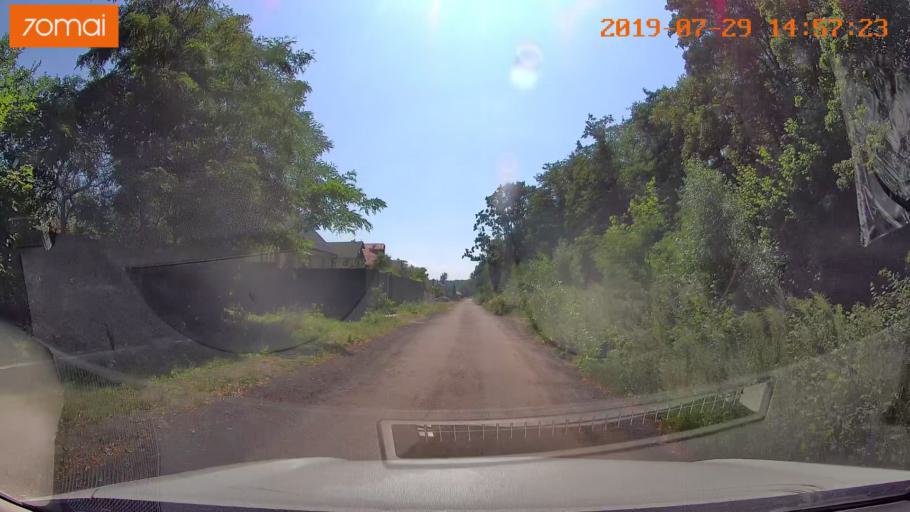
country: RU
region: Kaliningrad
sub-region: Gorod Kaliningrad
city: Baltiysk
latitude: 54.6804
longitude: 19.9168
